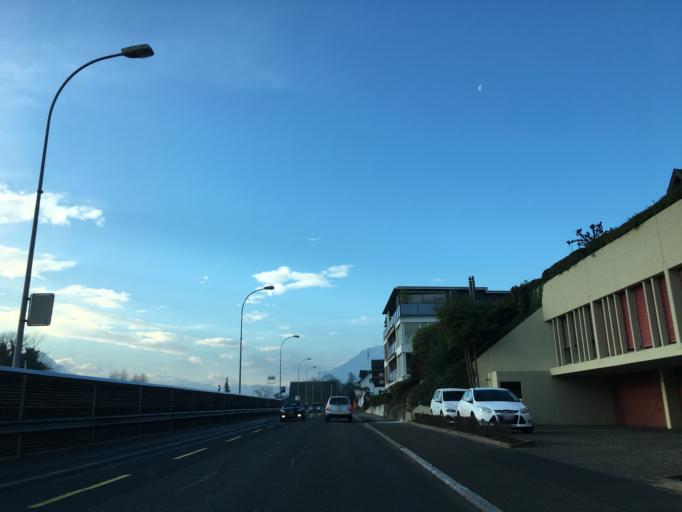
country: CH
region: Lucerne
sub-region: Lucerne-Land District
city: Udligenswil
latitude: 47.0629
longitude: 8.4043
